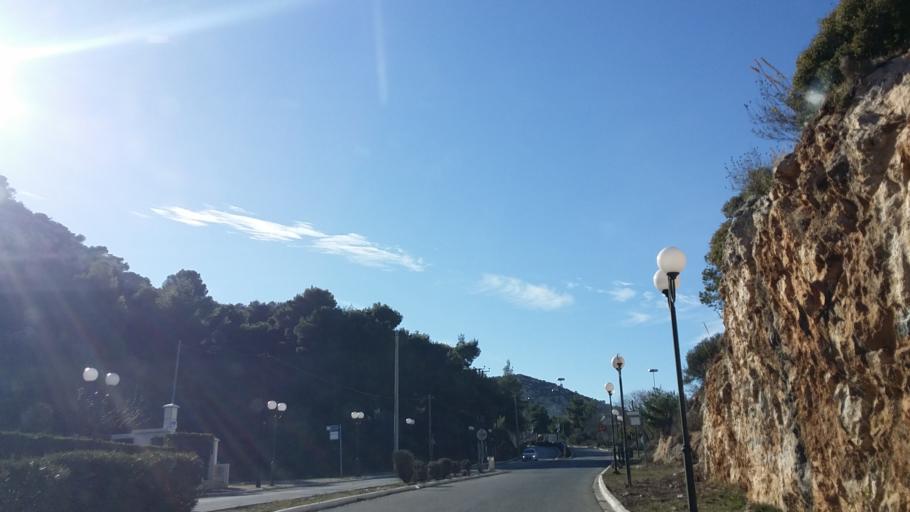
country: GR
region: Attica
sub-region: Nomarchia Dytikis Attikis
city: Fyli
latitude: 38.0998
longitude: 23.6752
